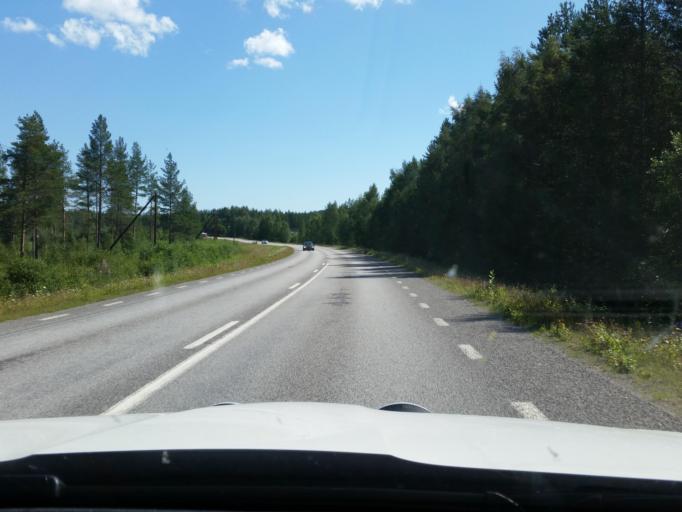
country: SE
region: Norrbotten
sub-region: Alvsbyns Kommun
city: AElvsbyn
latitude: 65.6897
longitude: 20.6903
